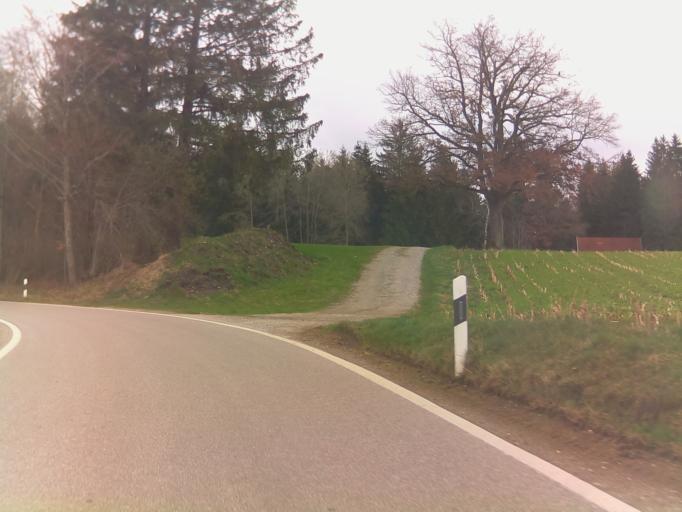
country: DE
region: Bavaria
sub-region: Upper Bavaria
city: Obersochering
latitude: 47.7463
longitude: 11.2210
